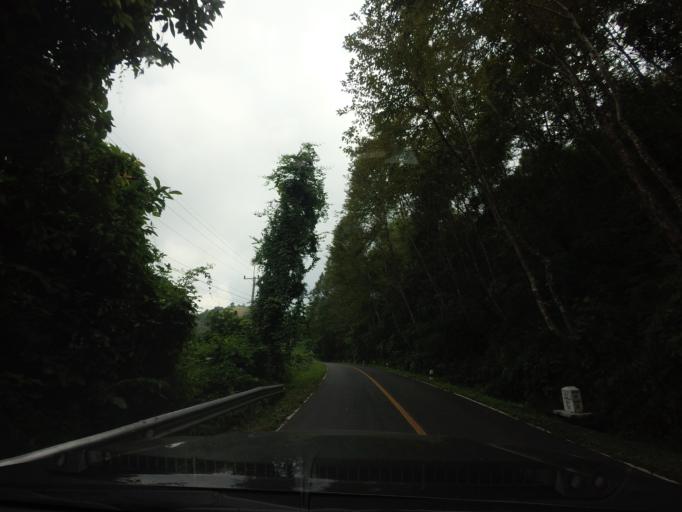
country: TH
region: Nan
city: Pua
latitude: 19.1887
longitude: 101.0198
